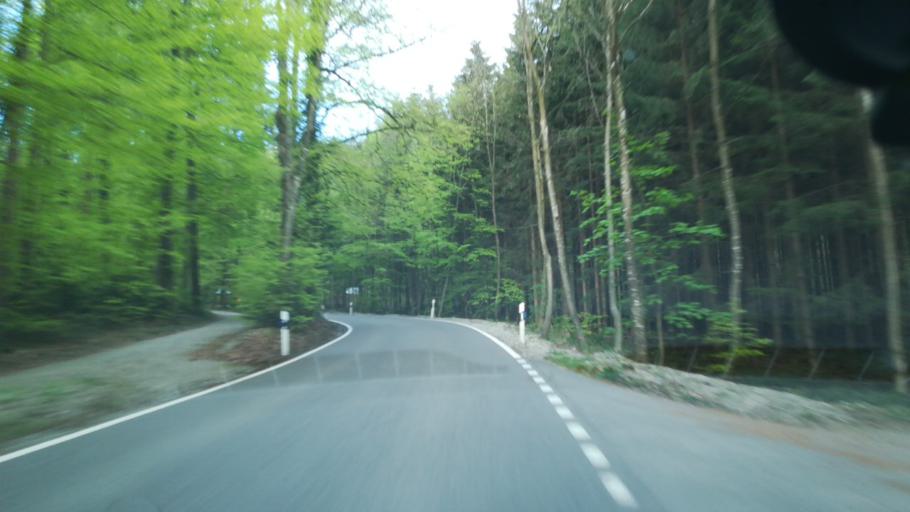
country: CH
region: Zurich
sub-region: Bezirk Uster
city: Gockhausen
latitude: 47.3724
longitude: 8.6029
